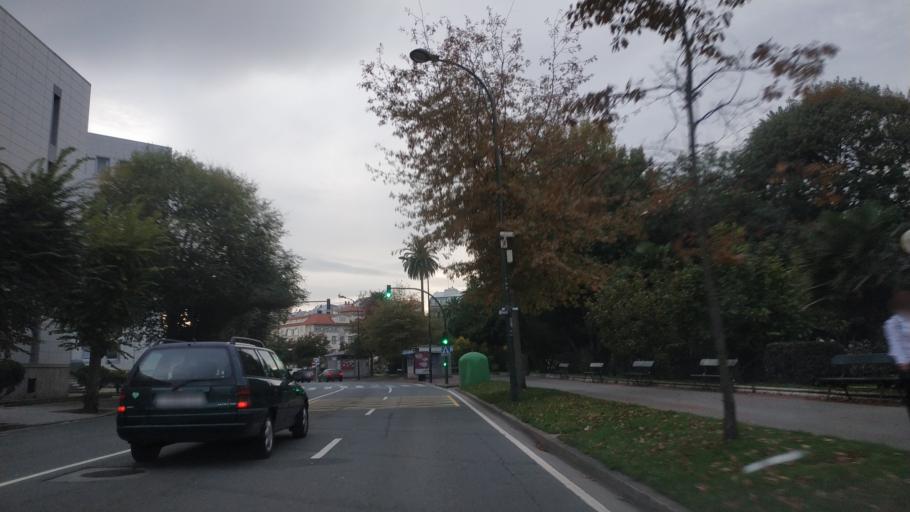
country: ES
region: Galicia
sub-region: Provincia da Coruna
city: A Coruna
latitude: 43.3666
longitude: -8.4031
